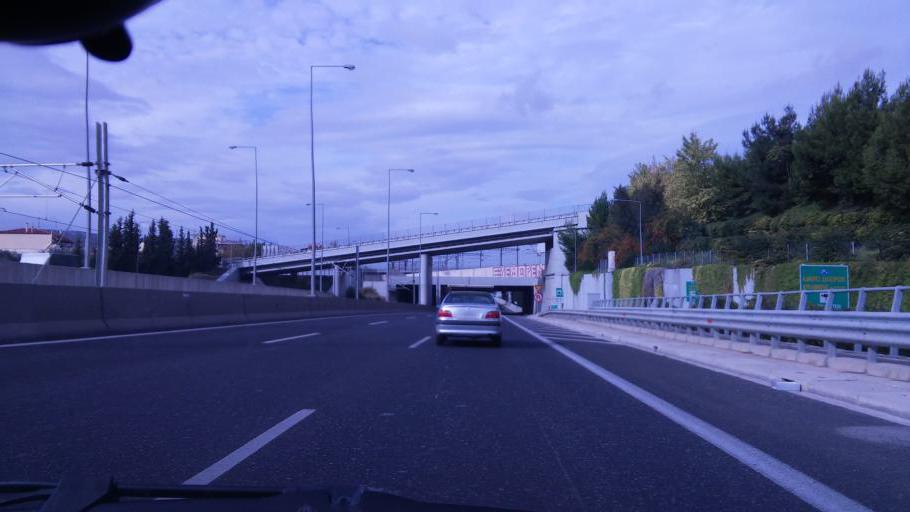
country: GR
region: Attica
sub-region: Nomarchia Dytikis Attikis
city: Zefyri
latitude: 38.0674
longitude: 23.7307
